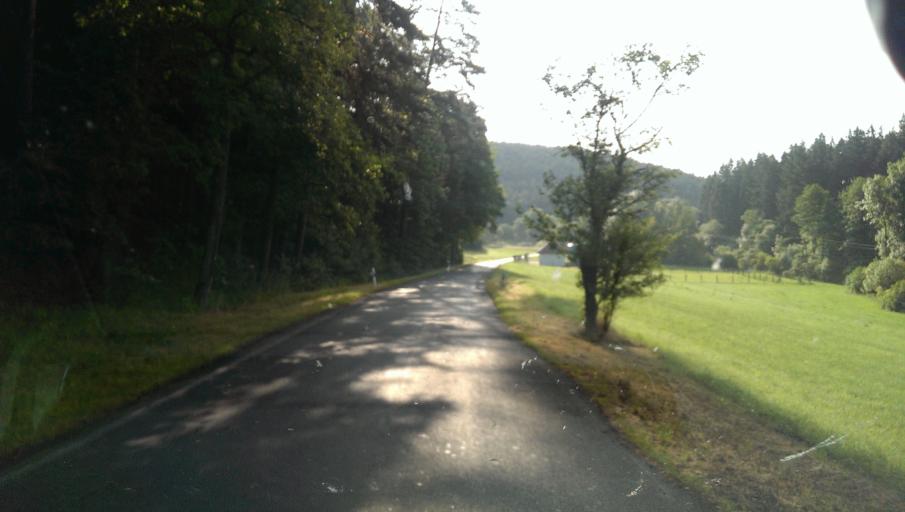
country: DE
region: Thuringia
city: Rottenbach
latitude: 50.7048
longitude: 11.1924
